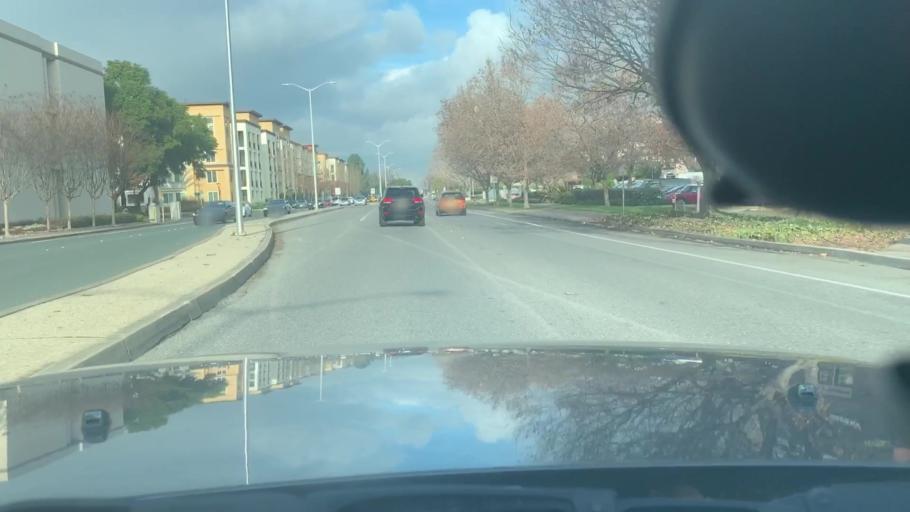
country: US
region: California
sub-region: Alameda County
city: Fremont
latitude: 37.5464
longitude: -121.9821
